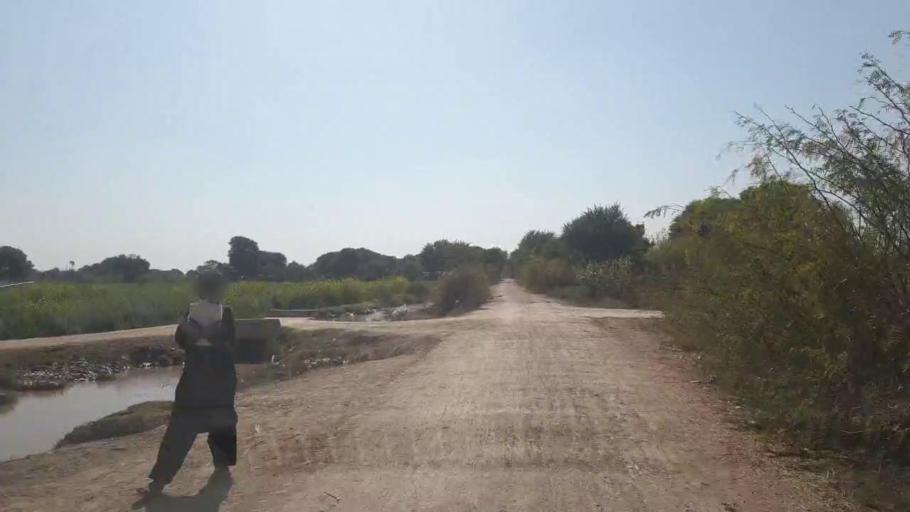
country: PK
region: Sindh
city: Chambar
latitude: 25.2932
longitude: 68.6872
